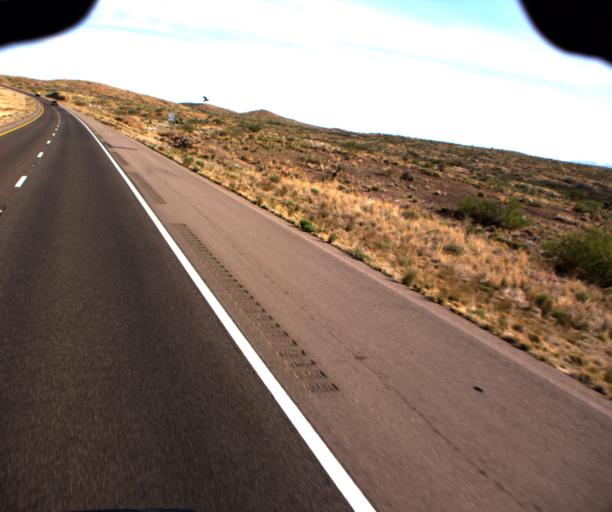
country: US
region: Arizona
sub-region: Cochise County
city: Willcox
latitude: 32.4476
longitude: -109.6634
